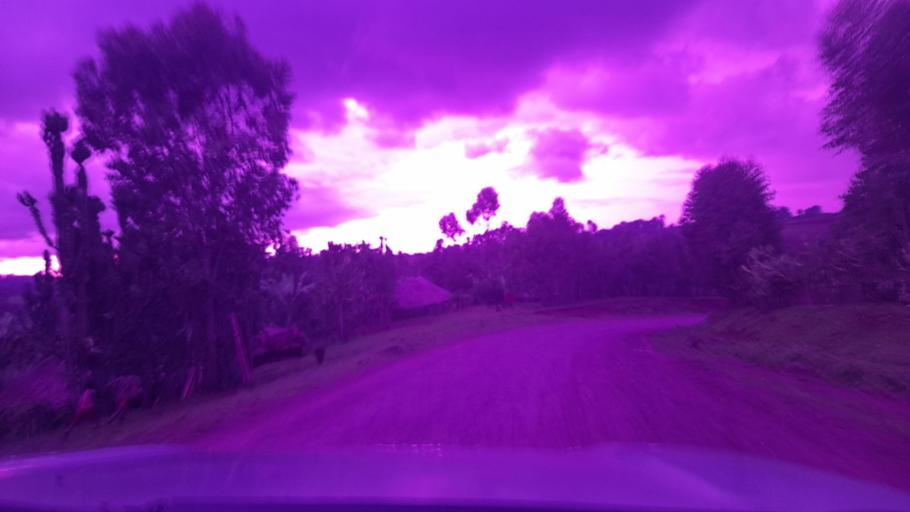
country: ET
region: Southern Nations, Nationalities, and People's Region
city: Mizan Teferi
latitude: 6.8902
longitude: 35.8493
